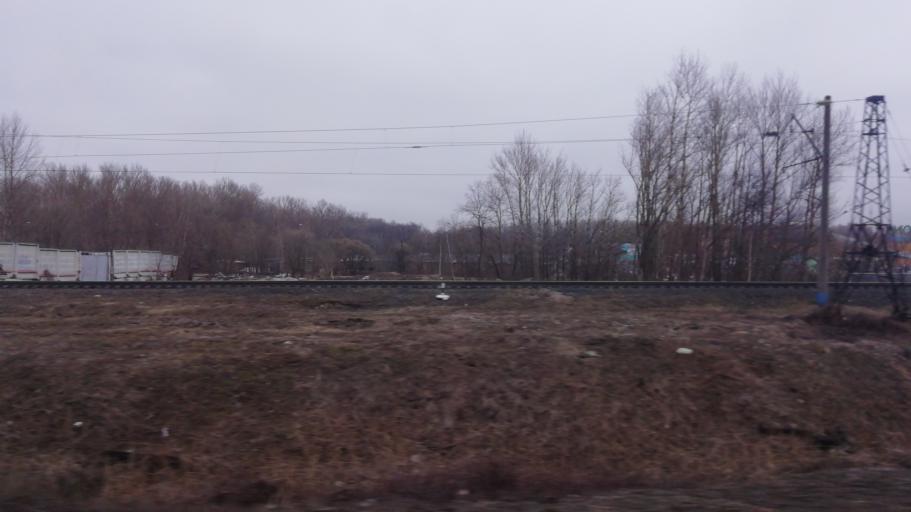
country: RU
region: St.-Petersburg
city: Kupchino
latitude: 59.8789
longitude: 30.3503
